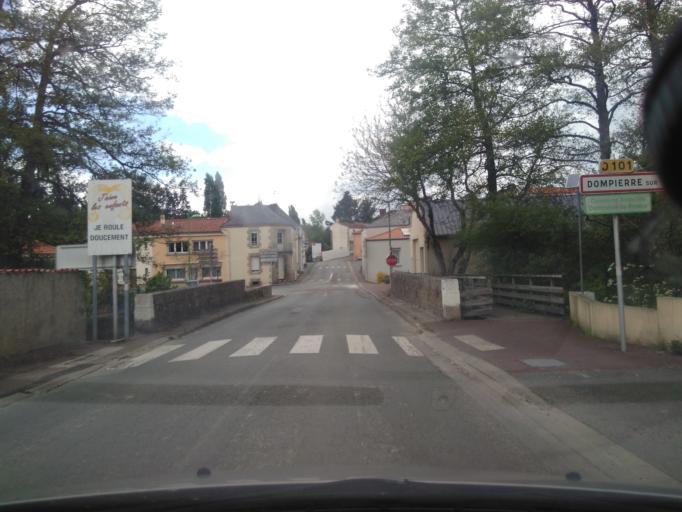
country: FR
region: Pays de la Loire
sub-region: Departement de la Vendee
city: Dompierre-sur-Yon
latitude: 46.7358
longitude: -1.3842
